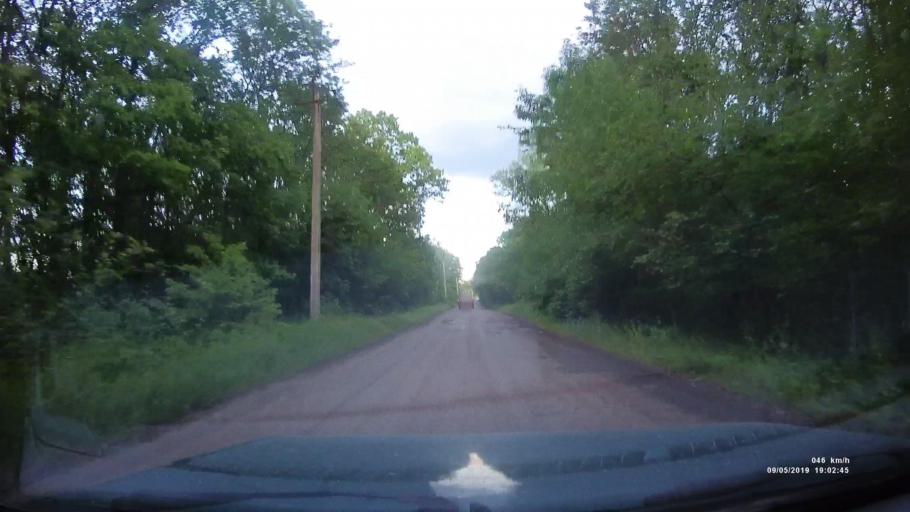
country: RU
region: Krasnodarskiy
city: Kanelovskaya
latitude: 46.7442
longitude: 39.1563
